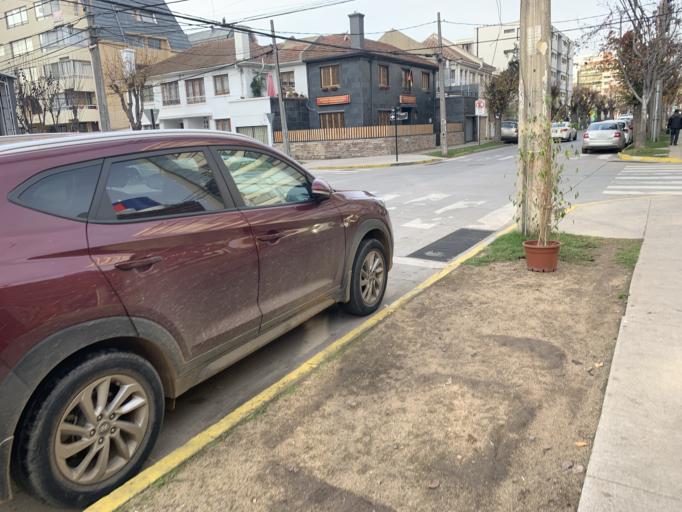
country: CL
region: Valparaiso
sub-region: Provincia de Valparaiso
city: Vina del Mar
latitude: -33.0207
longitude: -71.5577
